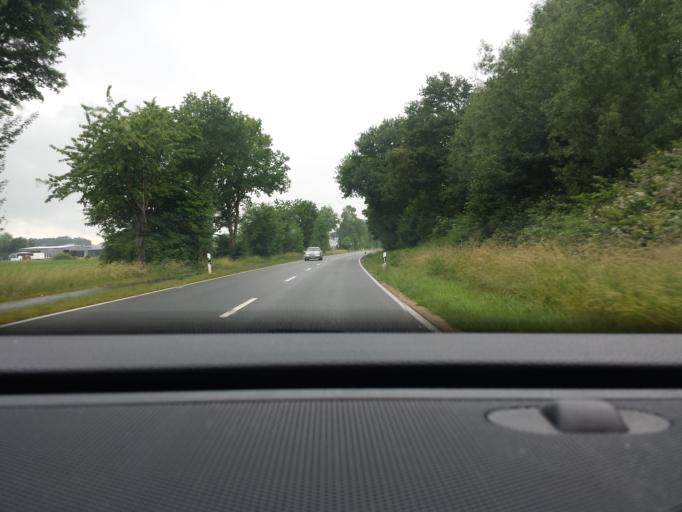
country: DE
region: North Rhine-Westphalia
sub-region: Regierungsbezirk Munster
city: Ahaus
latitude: 52.0732
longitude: 6.9710
